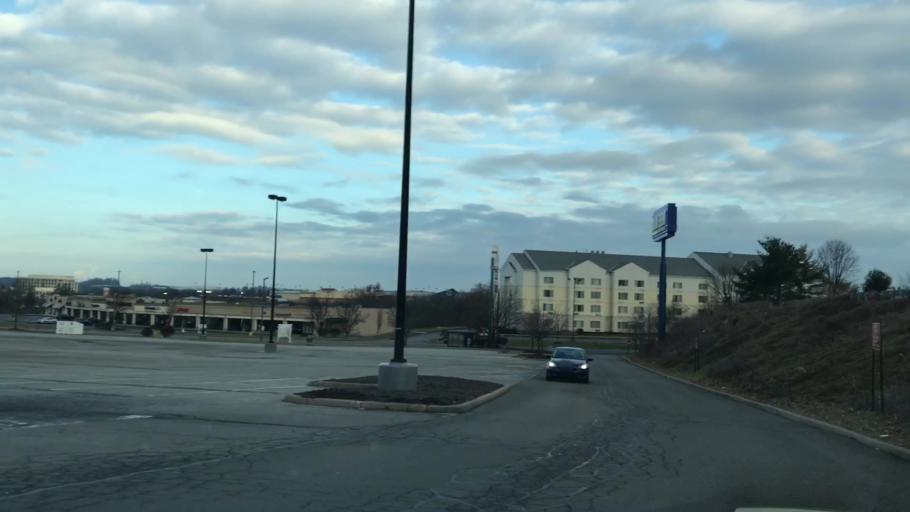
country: US
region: Pennsylvania
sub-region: Allegheny County
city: Oakdale
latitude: 40.4466
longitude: -80.1780
